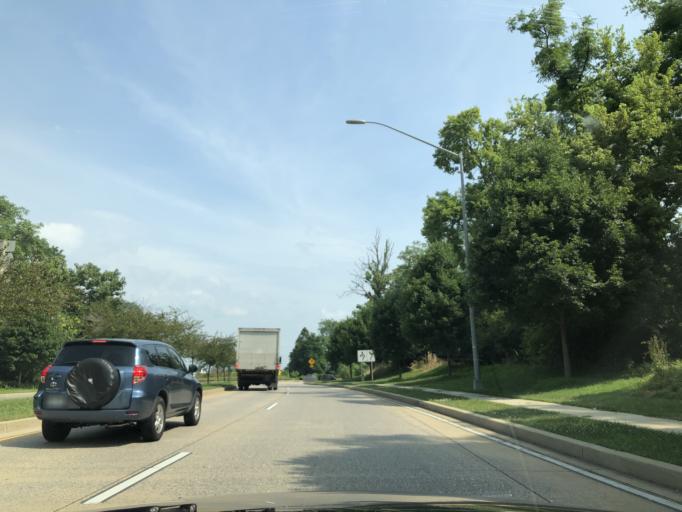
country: US
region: Maryland
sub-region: Frederick County
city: Frederick
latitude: 39.4048
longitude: -77.4036
